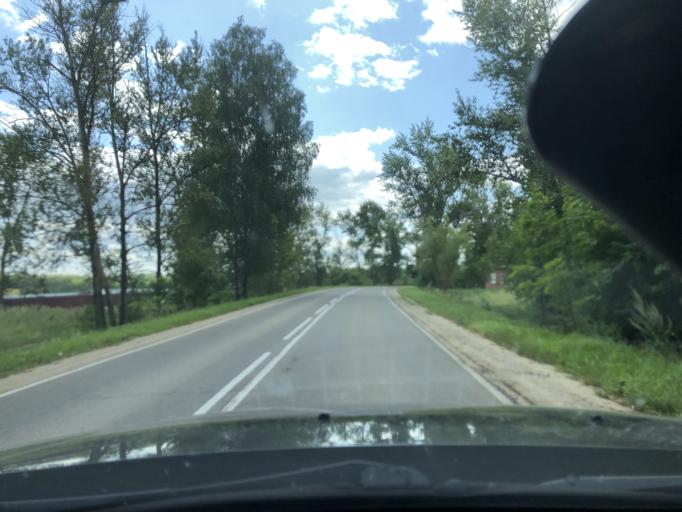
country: RU
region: Tula
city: Revyakino
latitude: 54.3553
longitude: 37.6345
